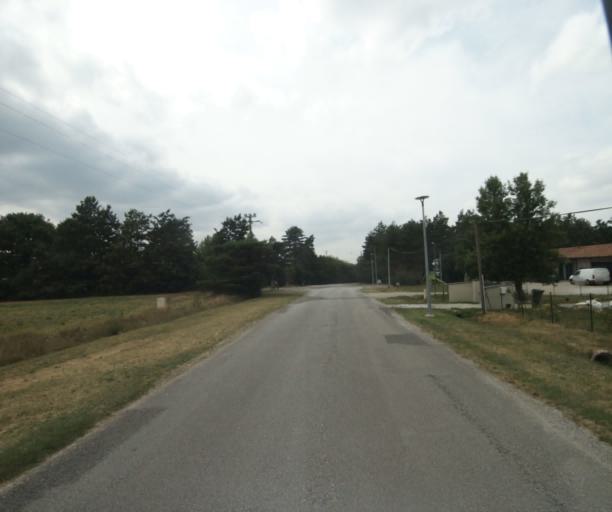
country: FR
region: Midi-Pyrenees
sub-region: Departement de la Haute-Garonne
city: Revel
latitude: 43.4321
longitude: 2.0181
